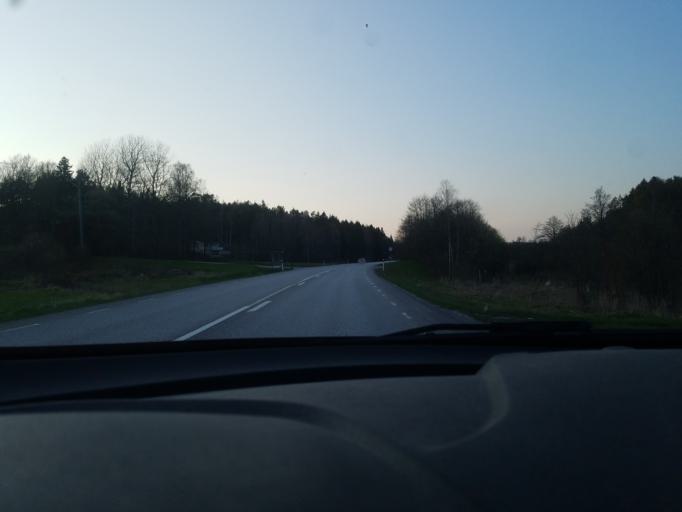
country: SE
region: Vaestra Goetaland
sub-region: Tjorns Kommun
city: Myggenas
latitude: 58.1463
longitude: 11.7074
